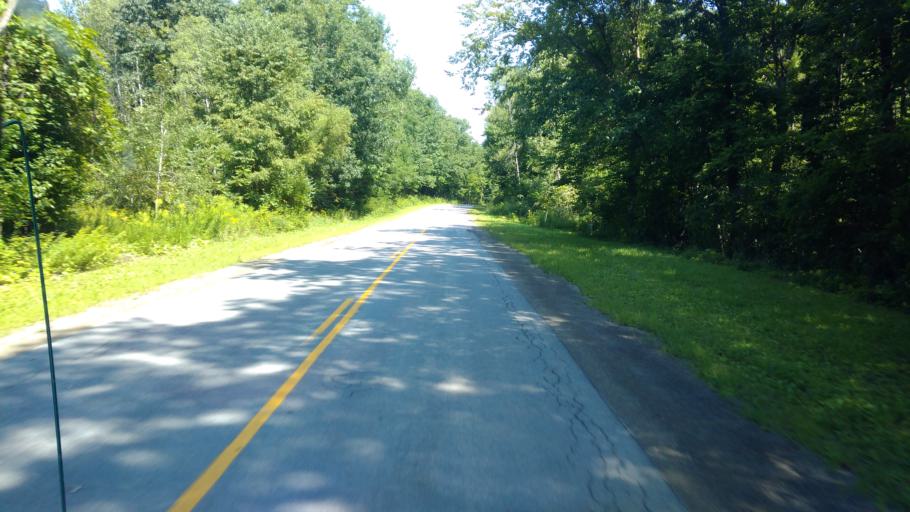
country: US
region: New York
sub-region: Allegany County
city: Belmont
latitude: 42.2833
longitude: -78.0552
